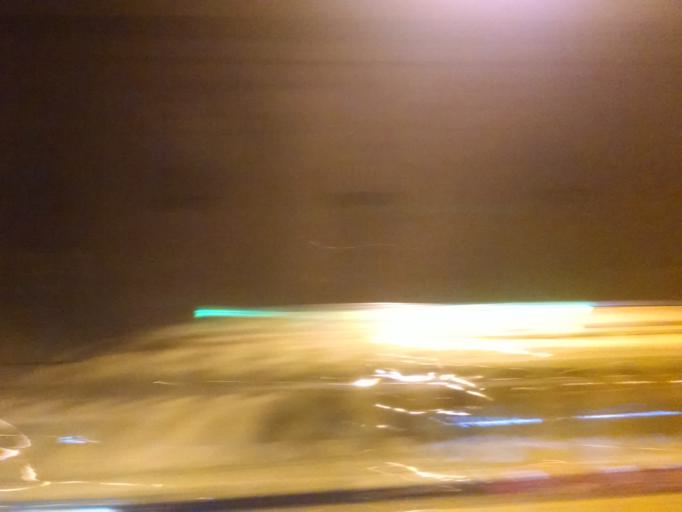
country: BR
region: Rio de Janeiro
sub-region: Rio De Janeiro
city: Rio de Janeiro
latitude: -22.9814
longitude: -43.2334
